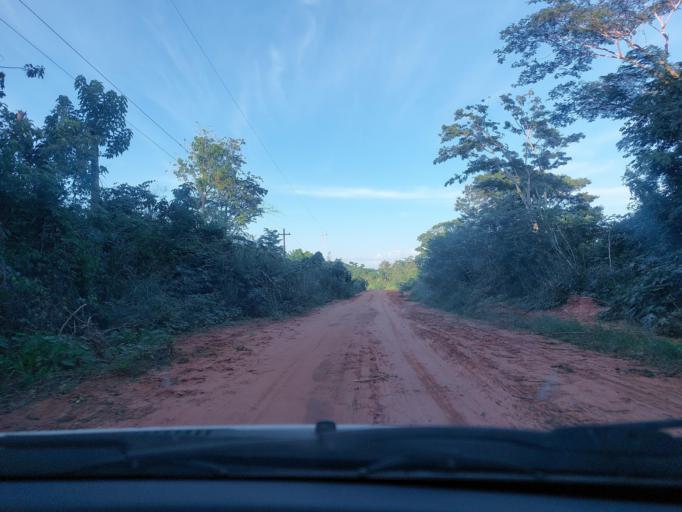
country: PY
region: San Pedro
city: Itacurubi del Rosario
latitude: -24.5409
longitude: -56.5827
